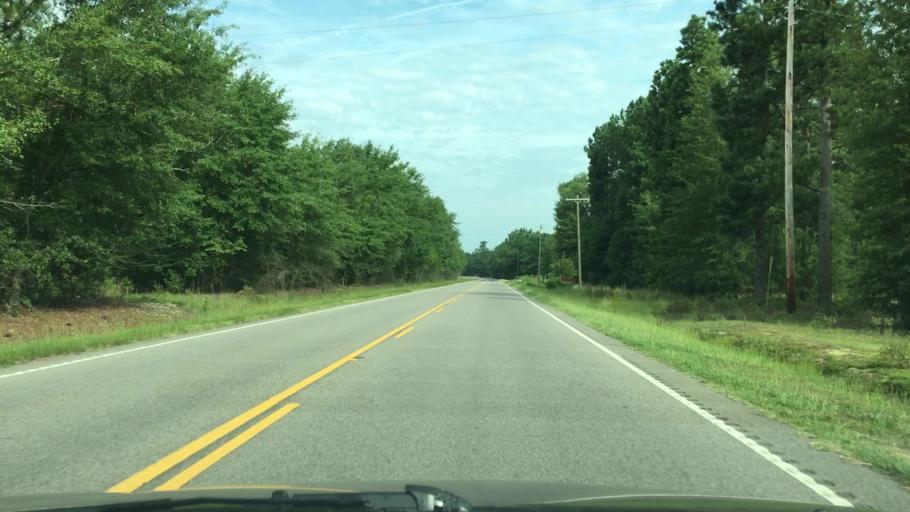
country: US
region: South Carolina
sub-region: Barnwell County
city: Williston
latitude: 33.6645
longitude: -81.3946
